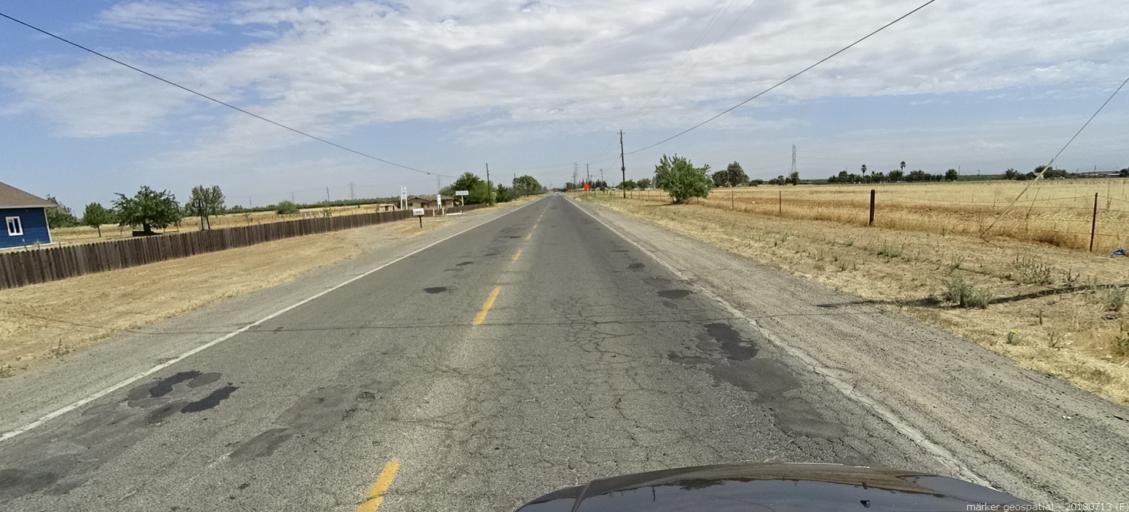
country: US
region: California
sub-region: Madera County
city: Madera Acres
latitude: 36.9934
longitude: -120.0562
